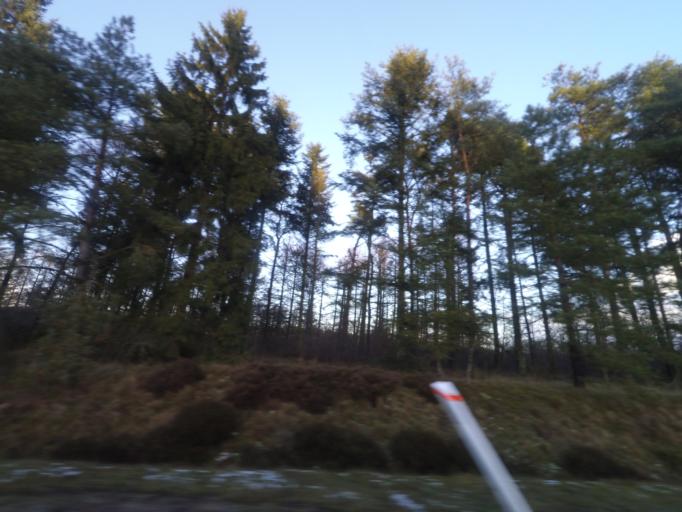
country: DK
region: Central Jutland
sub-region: Ikast-Brande Kommune
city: Brande
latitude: 56.0015
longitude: 9.1786
